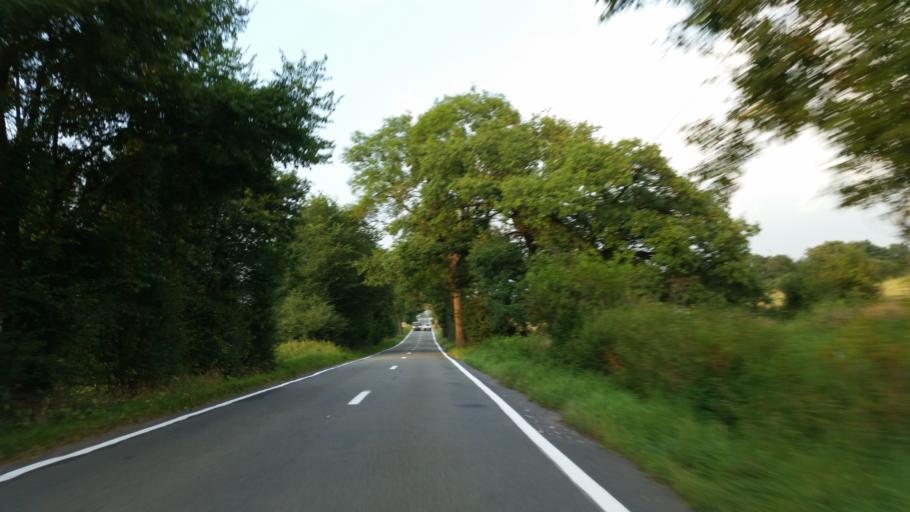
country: BE
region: Wallonia
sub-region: Province de Namur
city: Somme-Leuze
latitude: 50.3147
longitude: 5.4067
